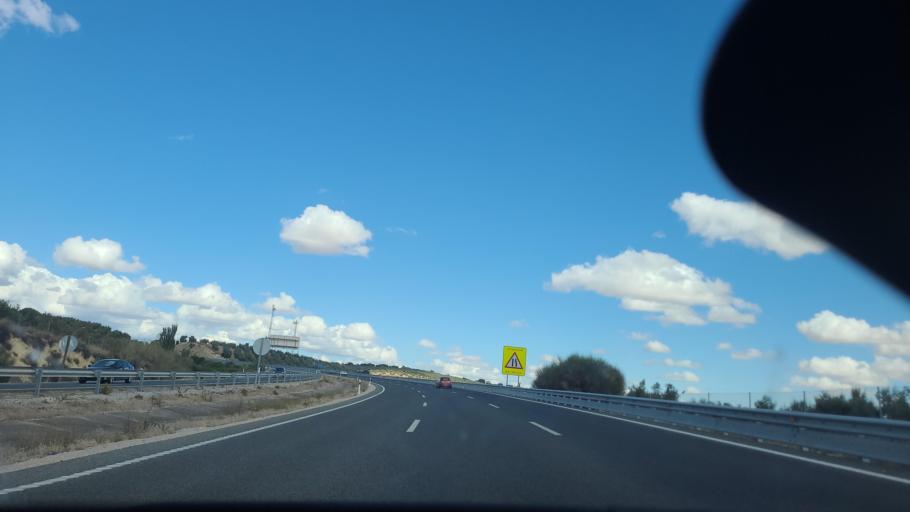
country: ES
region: Andalusia
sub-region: Provincia de Granada
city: Iznalloz
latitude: 37.4166
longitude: -3.5568
